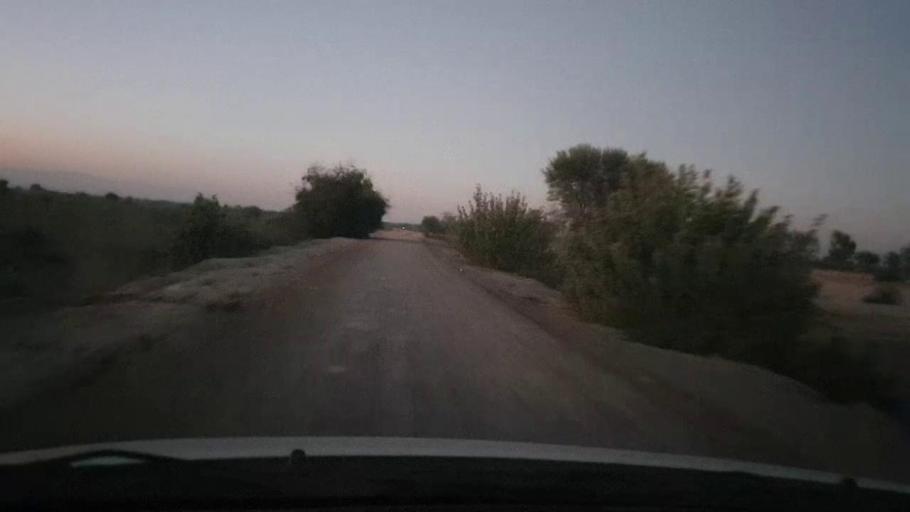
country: PK
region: Sindh
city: Phulji
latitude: 26.9044
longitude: 67.4707
